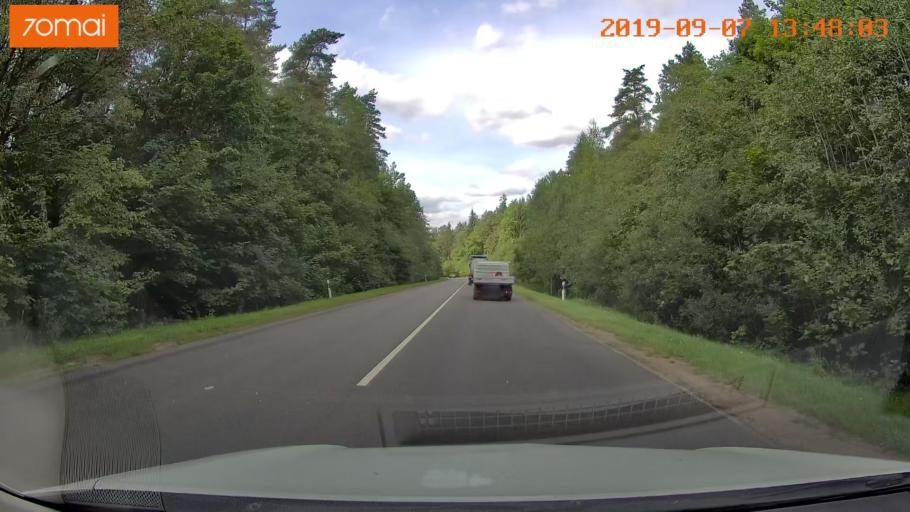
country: LT
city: Baltoji Voke
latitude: 54.6005
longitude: 25.2071
